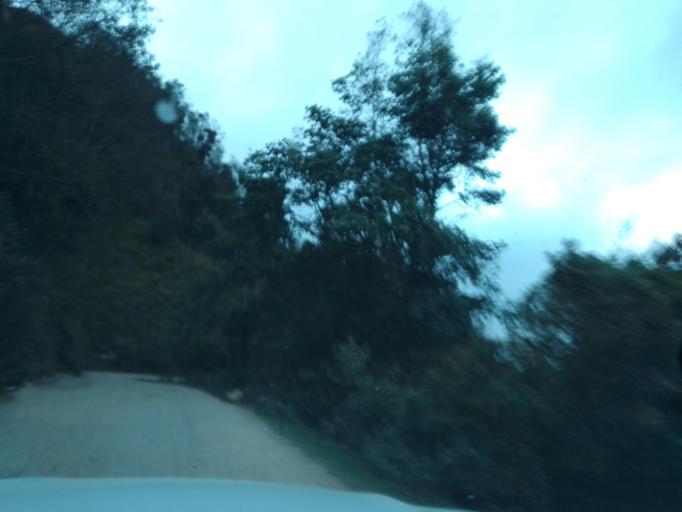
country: MX
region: Chiapas
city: Motozintla de Mendoza
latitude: 15.2194
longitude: -92.2373
